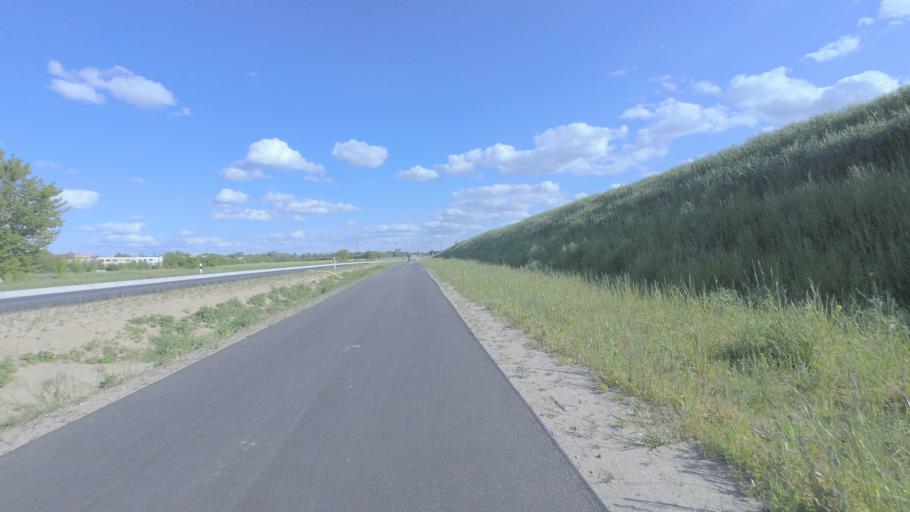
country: DE
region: Brandenburg
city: Stahnsdorf
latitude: 52.3828
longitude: 13.2319
